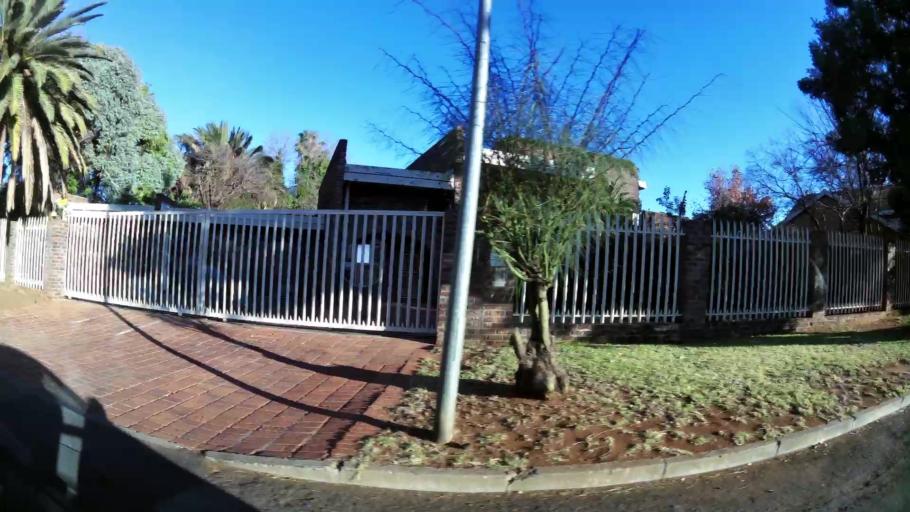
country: ZA
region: Northern Cape
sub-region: Frances Baard District Municipality
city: Kimberley
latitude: -28.7611
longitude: 24.7579
